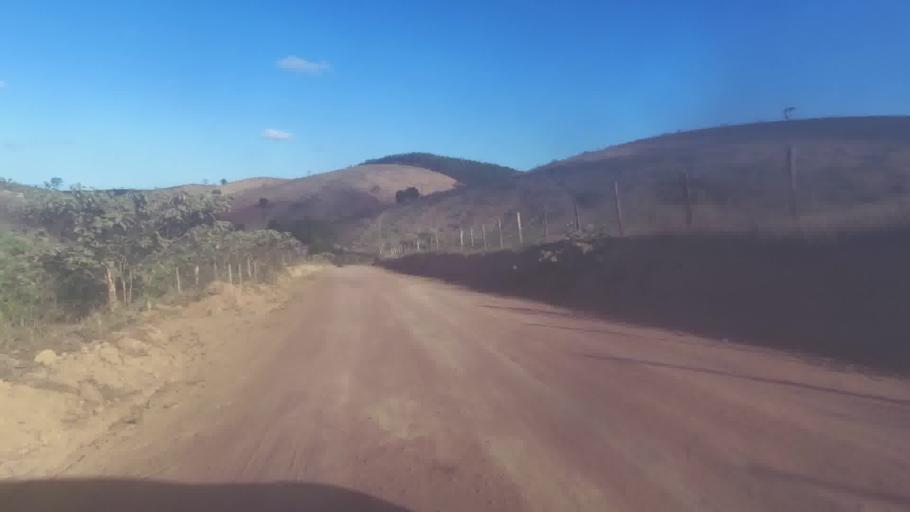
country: BR
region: Espirito Santo
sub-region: Mimoso Do Sul
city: Mimoso do Sul
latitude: -21.0929
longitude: -41.1397
